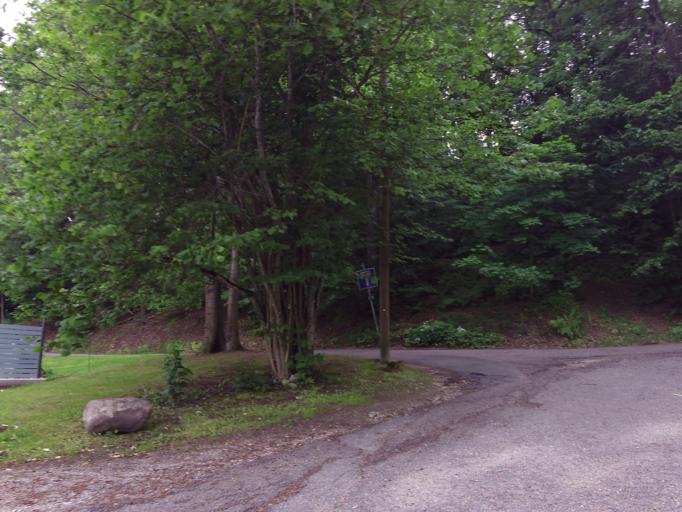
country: EE
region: Harju
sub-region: Saue vald
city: Laagri
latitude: 59.3891
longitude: 24.6610
